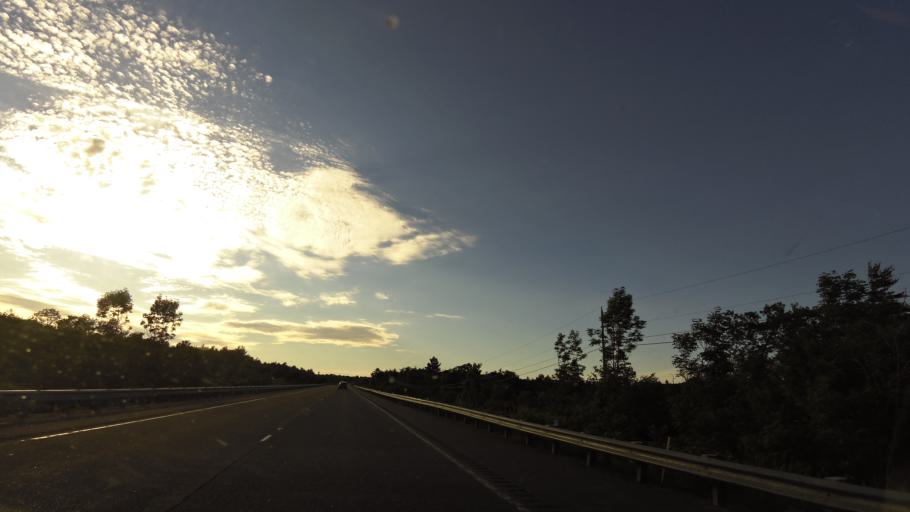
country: CA
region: Ontario
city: Midland
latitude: 44.8951
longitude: -79.7609
